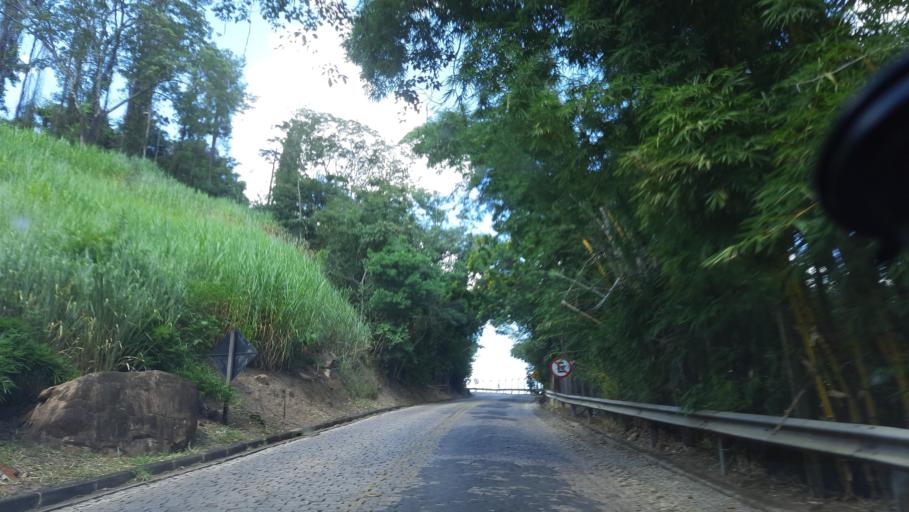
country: BR
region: Sao Paulo
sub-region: Sao Jose Do Rio Pardo
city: Sao Jose do Rio Pardo
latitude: -21.6024
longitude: -46.9517
